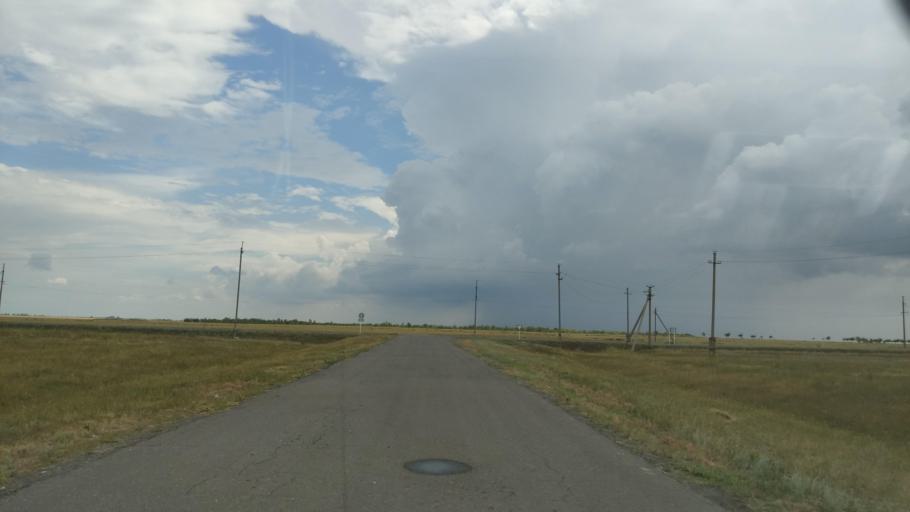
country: KZ
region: Pavlodar
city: Pavlodar
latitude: 52.6330
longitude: 77.3466
